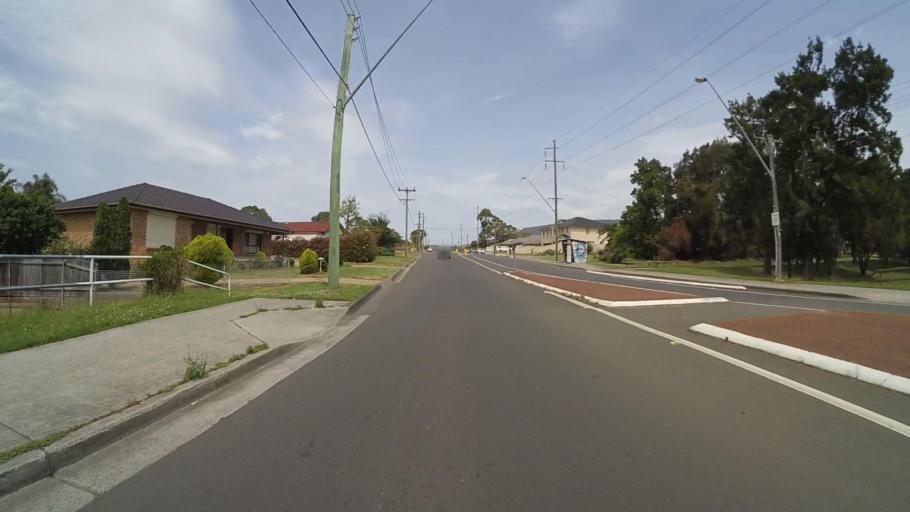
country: AU
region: New South Wales
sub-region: Shellharbour
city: Albion Park Rail
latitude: -34.5757
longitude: 150.7764
